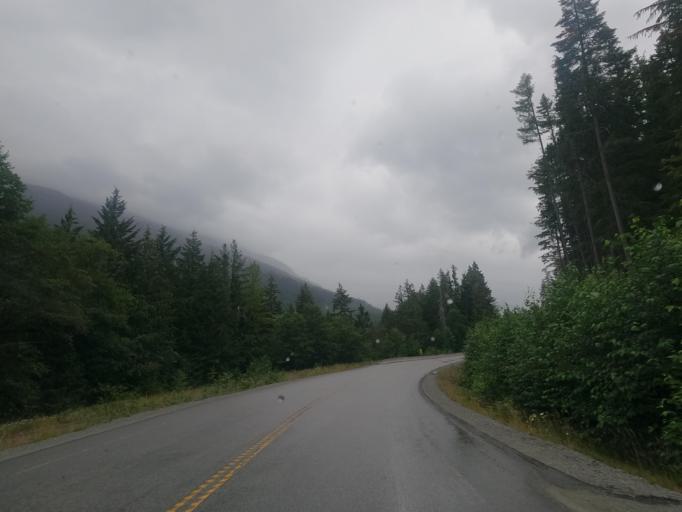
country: CA
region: British Columbia
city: Pemberton
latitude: 50.3262
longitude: -122.5562
